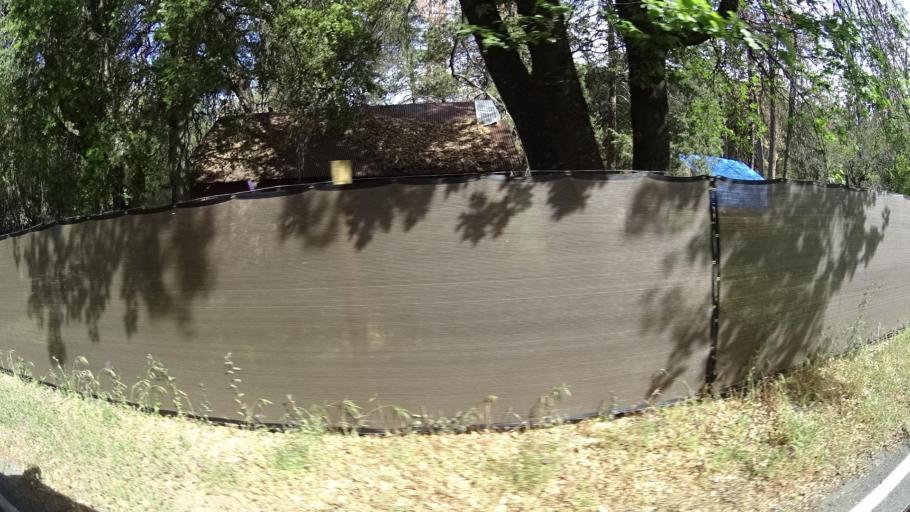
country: US
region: California
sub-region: Lake County
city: Soda Bay
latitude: 38.9117
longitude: -122.7622
